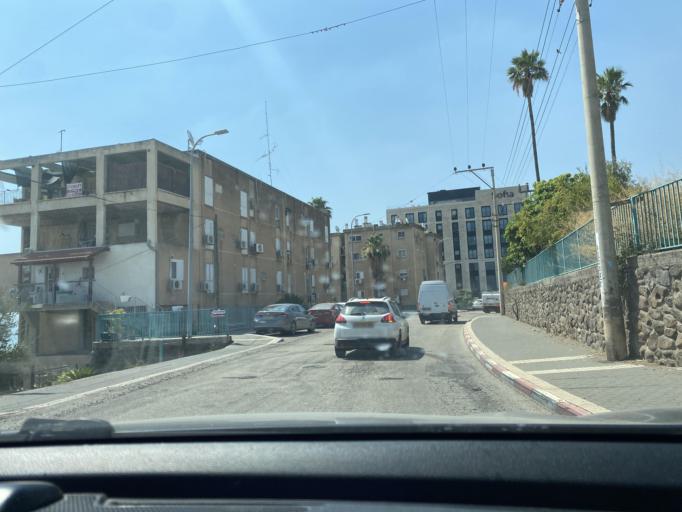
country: IL
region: Northern District
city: Tiberias
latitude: 32.7930
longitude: 35.5400
